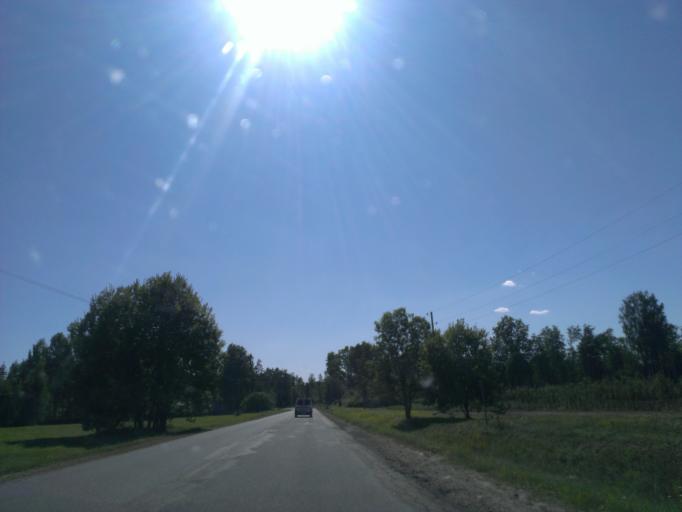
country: LV
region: Sigulda
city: Sigulda
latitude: 57.1267
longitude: 24.8313
